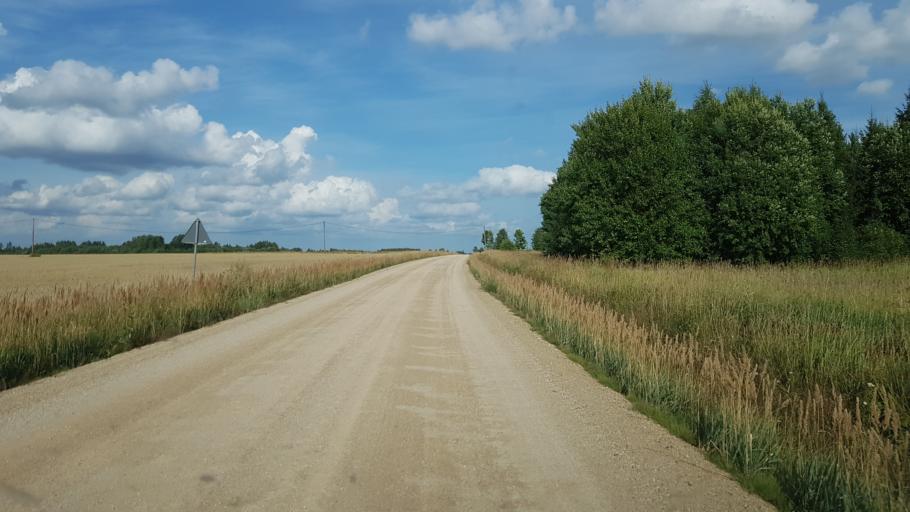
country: RU
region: Pskov
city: Pechory
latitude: 57.7909
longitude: 27.4786
